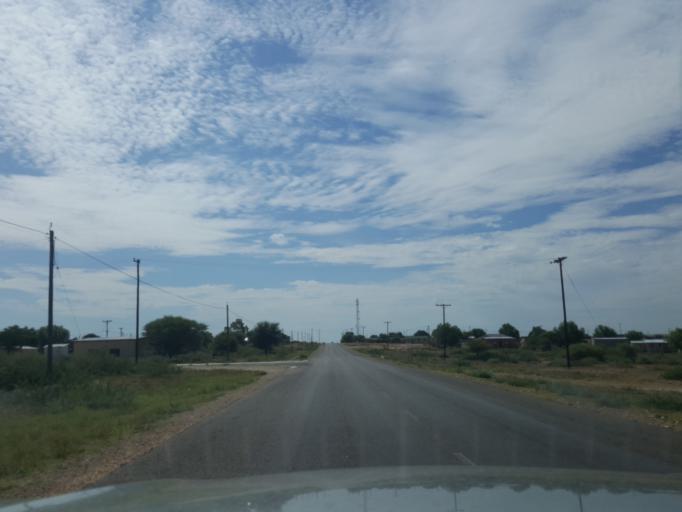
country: BW
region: Kweneng
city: Letlhakeng
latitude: -24.1086
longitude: 25.0338
